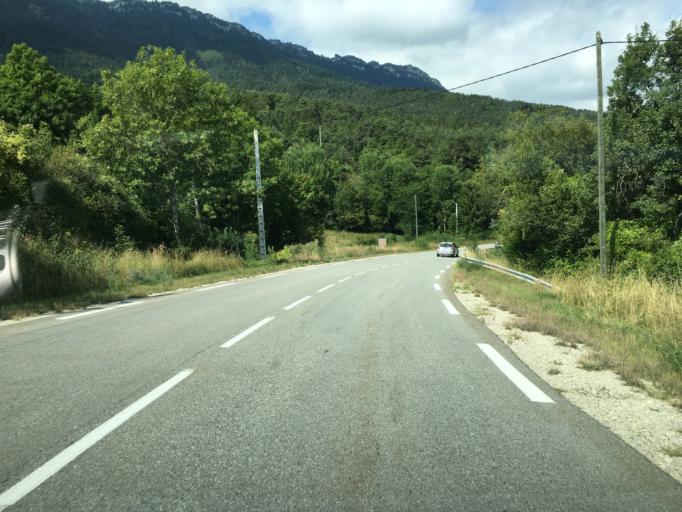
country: FR
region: Rhone-Alpes
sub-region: Departement de l'Isere
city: Mens
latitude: 44.8036
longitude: 5.6314
